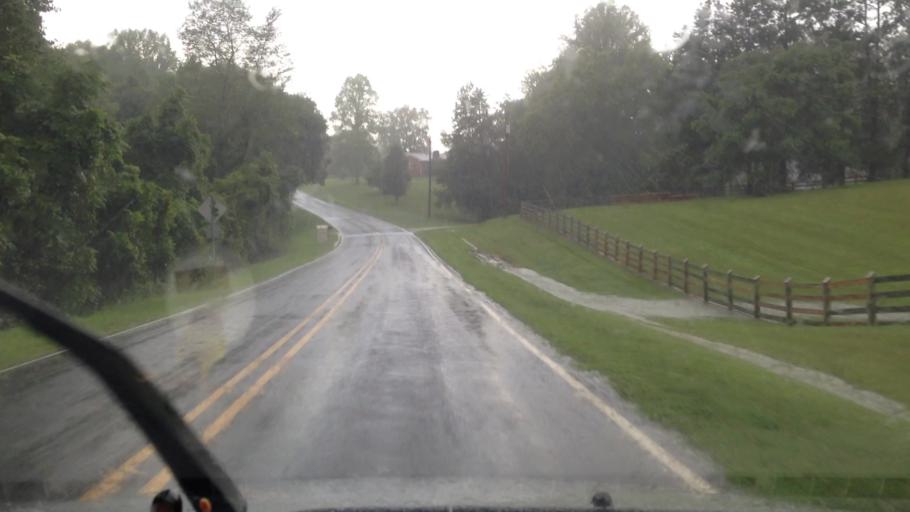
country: US
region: North Carolina
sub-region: Guilford County
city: Oak Ridge
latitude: 36.2084
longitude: -80.0237
